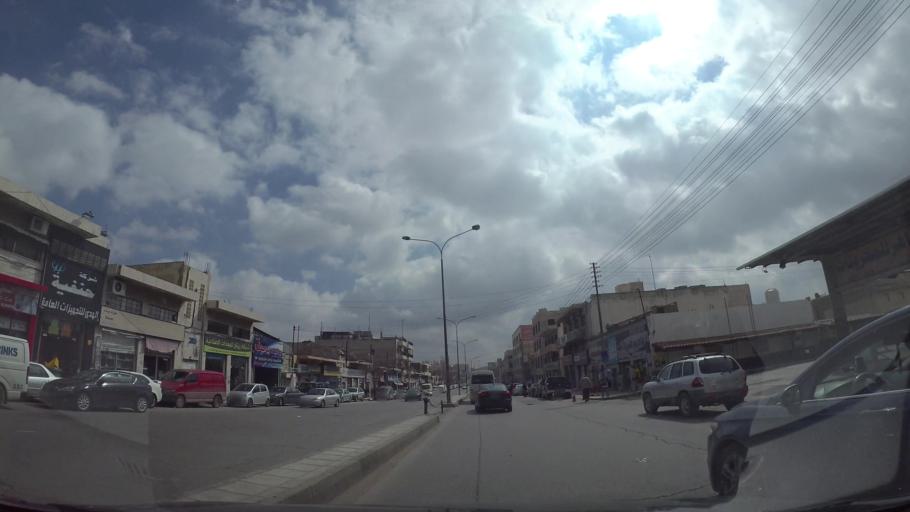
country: JO
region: Amman
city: Al Quwaysimah
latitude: 31.9263
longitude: 35.9378
